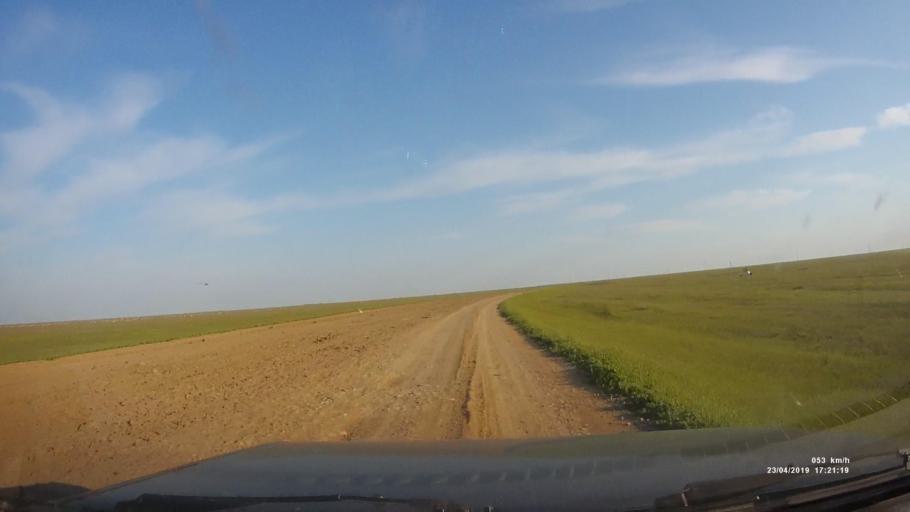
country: RU
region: Kalmykiya
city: Priyutnoye
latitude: 46.1771
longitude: 43.5049
